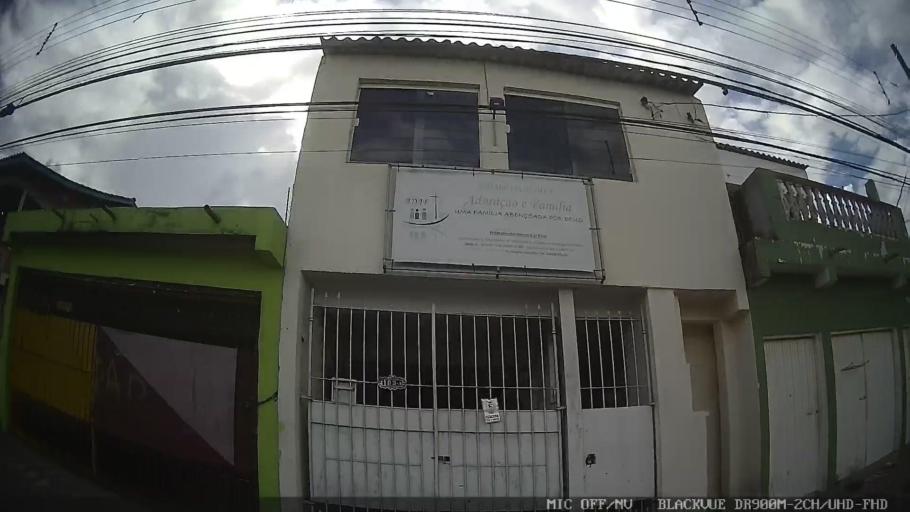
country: BR
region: Sao Paulo
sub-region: Mogi das Cruzes
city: Mogi das Cruzes
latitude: -23.5450
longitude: -46.2461
